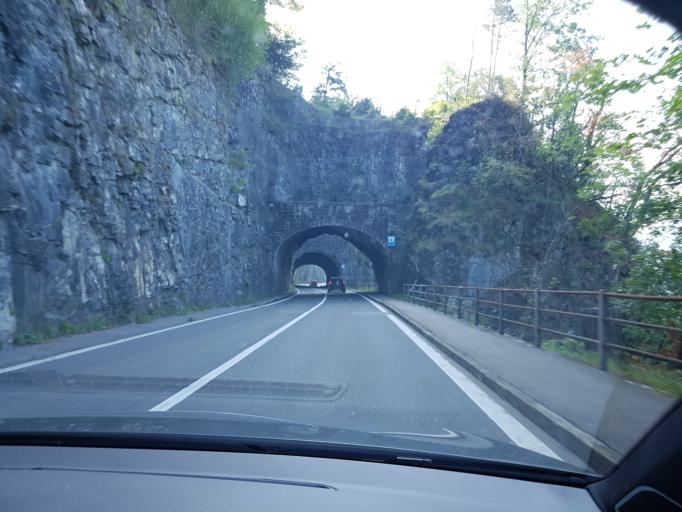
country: CH
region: Schwyz
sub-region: Bezirk Schwyz
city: Ingenbohl
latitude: 46.9787
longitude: 8.6116
